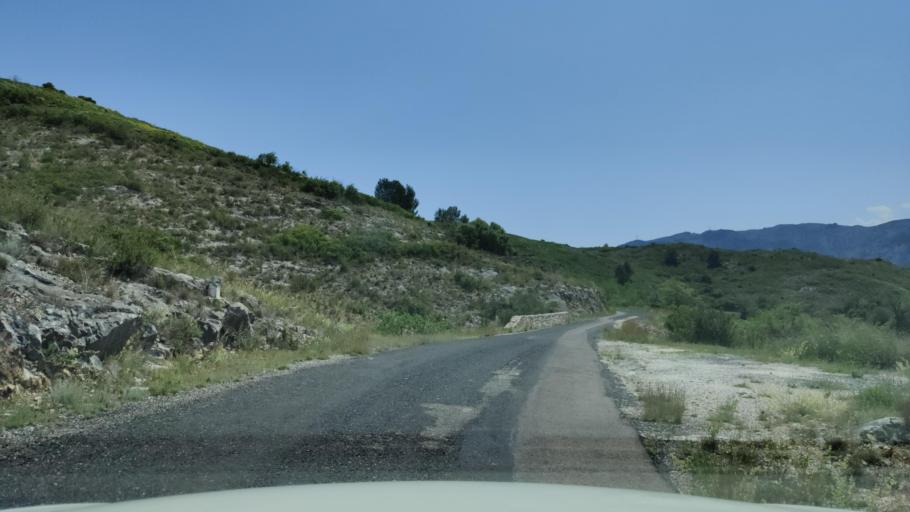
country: FR
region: Languedoc-Roussillon
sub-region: Departement des Pyrenees-Orientales
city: Estagel
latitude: 42.7875
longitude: 2.7519
